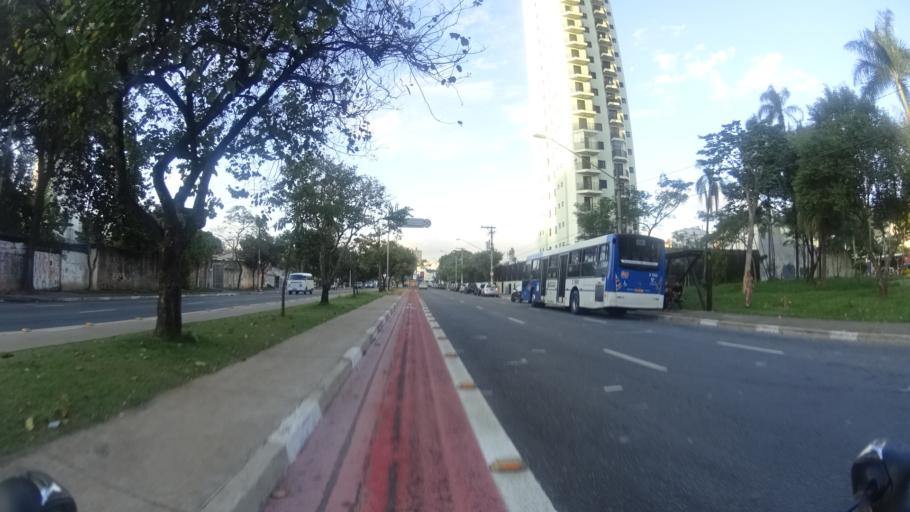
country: BR
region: Sao Paulo
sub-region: Sao Paulo
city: Sao Paulo
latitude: -23.4821
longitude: -46.6301
